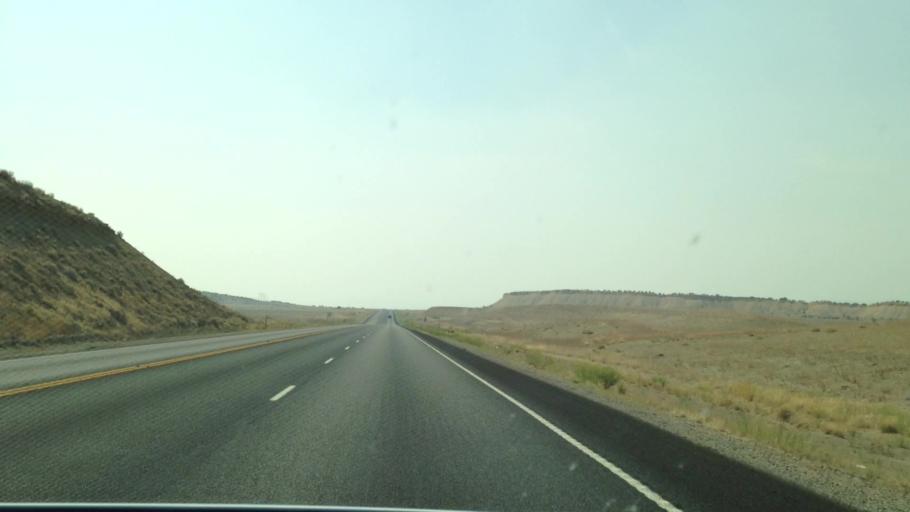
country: US
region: Utah
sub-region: Carbon County
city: Wellington
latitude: 39.5394
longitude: -110.6086
